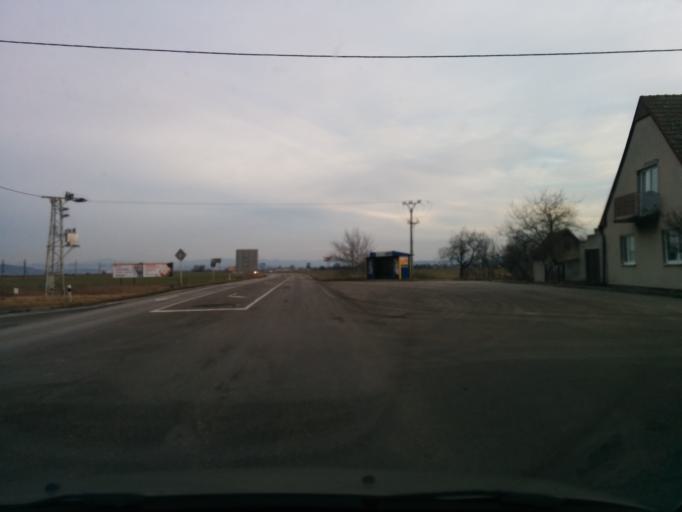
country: SK
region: Trnavsky
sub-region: Okres Trnava
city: Piestany
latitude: 48.6602
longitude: 17.8418
